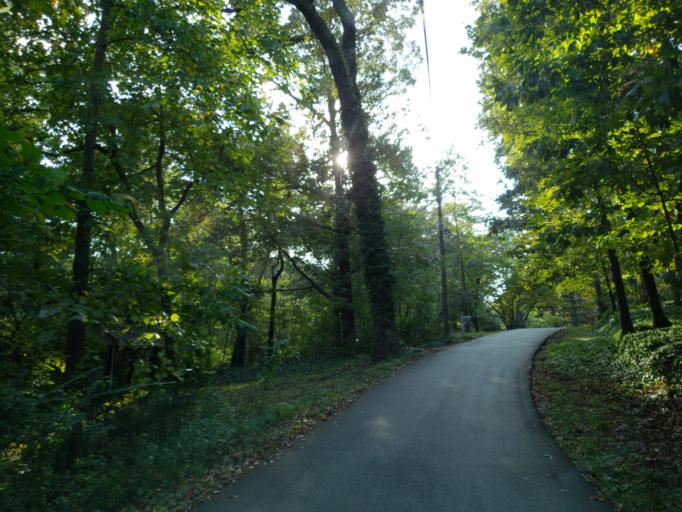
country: US
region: Georgia
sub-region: Fulton County
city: Roswell
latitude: 34.0799
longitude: -84.4062
